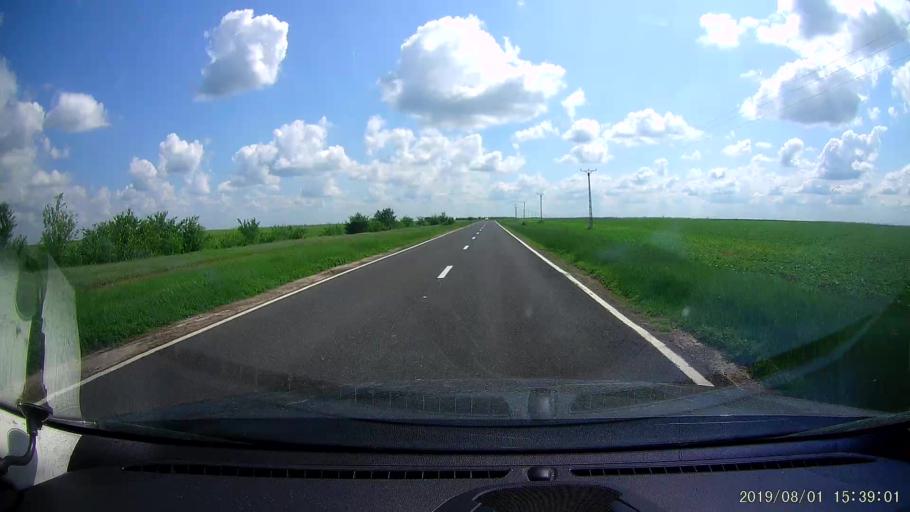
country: RO
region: Braila
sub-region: Comuna Insuratei
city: Insuratei
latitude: 44.8677
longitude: 27.5675
